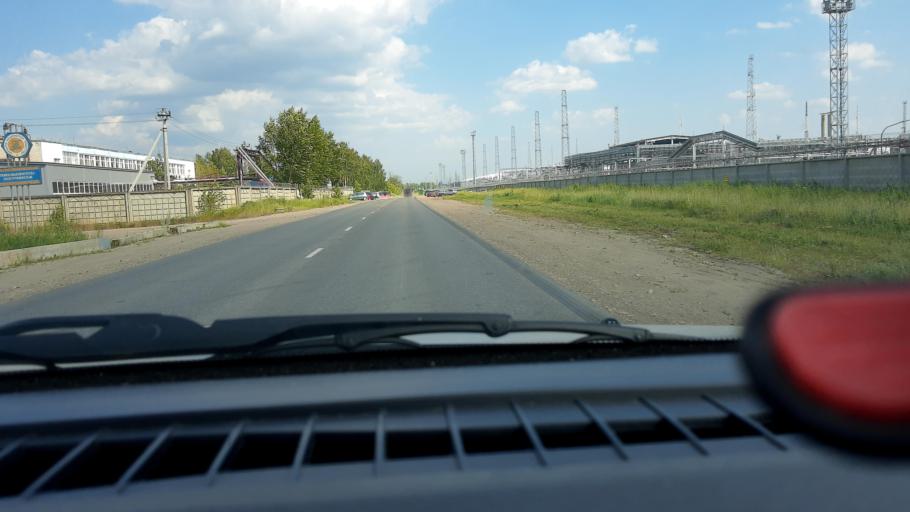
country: RU
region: Nizjnij Novgorod
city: Kstovo
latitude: 56.1229
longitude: 44.1318
